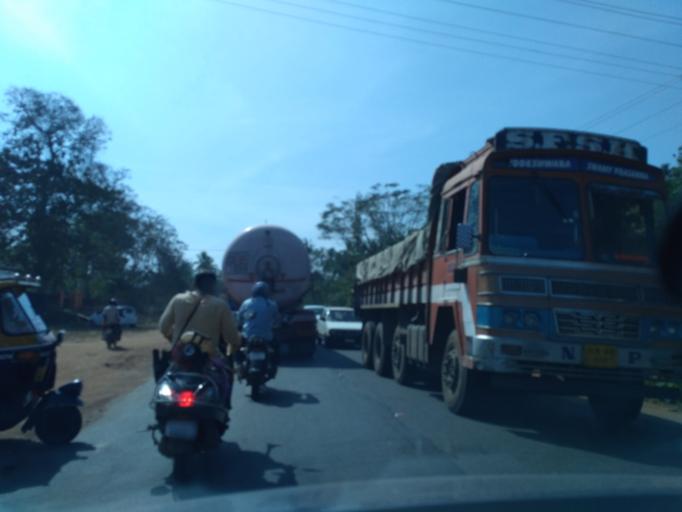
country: IN
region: Karnataka
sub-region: Dakshina Kannada
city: Bantval
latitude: 12.8728
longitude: 75.0475
